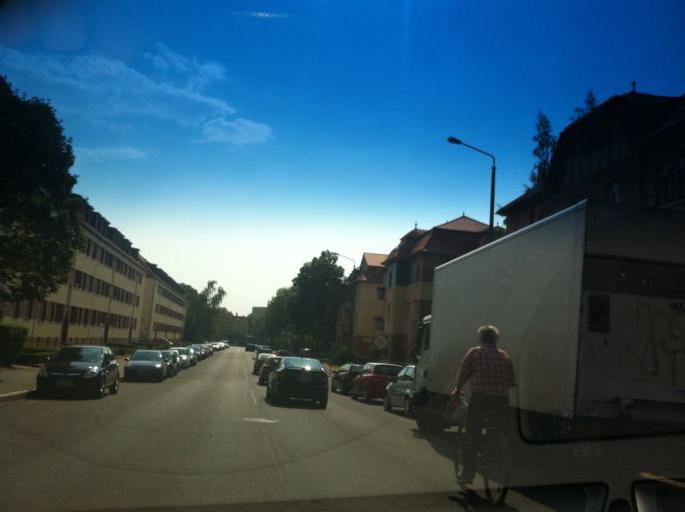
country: DE
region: Saxony
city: Markkleeberg
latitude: 51.2989
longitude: 12.3923
